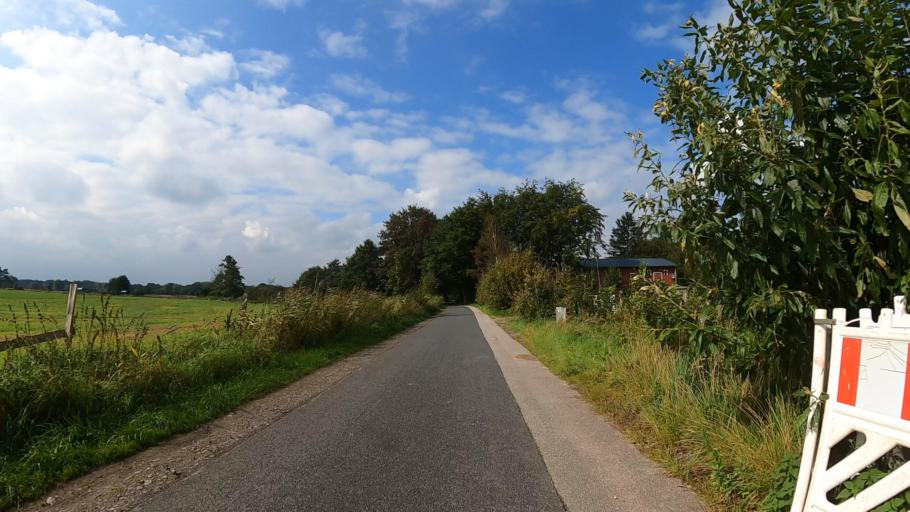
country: DE
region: Schleswig-Holstein
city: Tornesch
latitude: 53.7212
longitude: 9.7005
